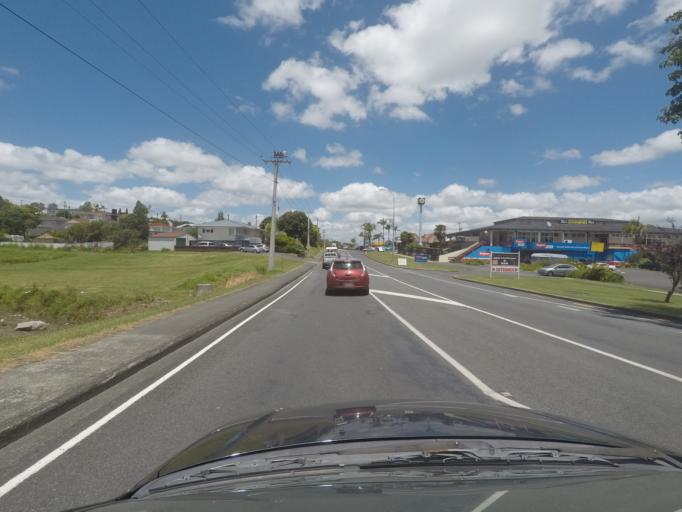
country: NZ
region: Northland
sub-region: Whangarei
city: Whangarei
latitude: -35.7533
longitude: 174.3683
